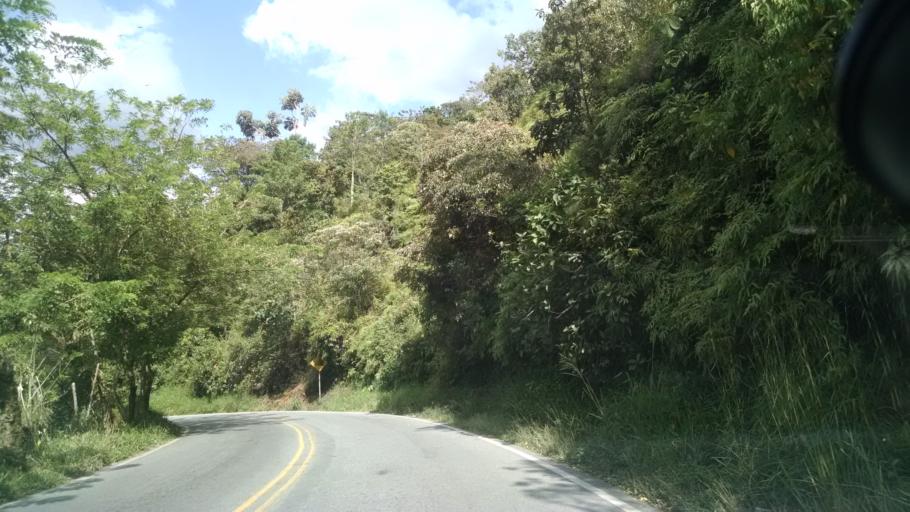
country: CO
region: Antioquia
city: Santo Domingo
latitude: 6.5325
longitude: -75.2346
